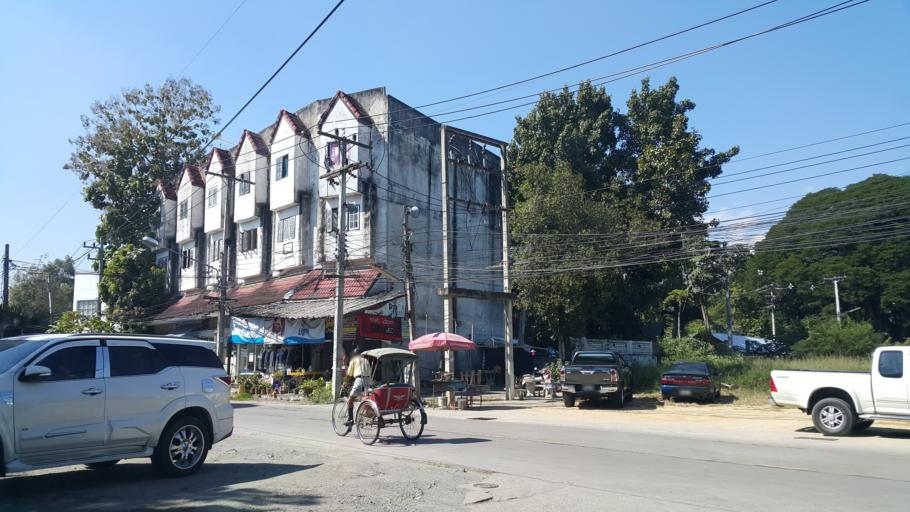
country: TH
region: Chiang Mai
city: Chiang Mai
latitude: 18.7612
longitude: 99.0047
